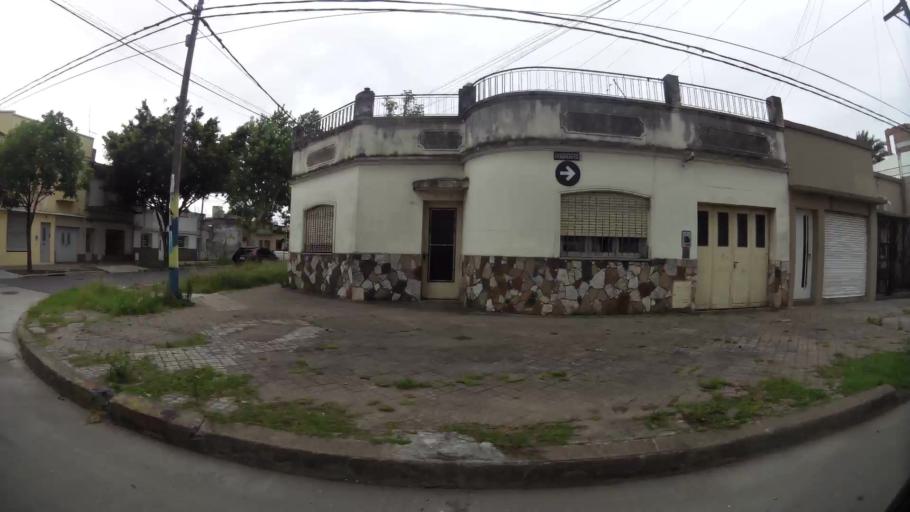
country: AR
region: Santa Fe
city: Gobernador Galvez
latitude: -32.9885
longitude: -60.6532
